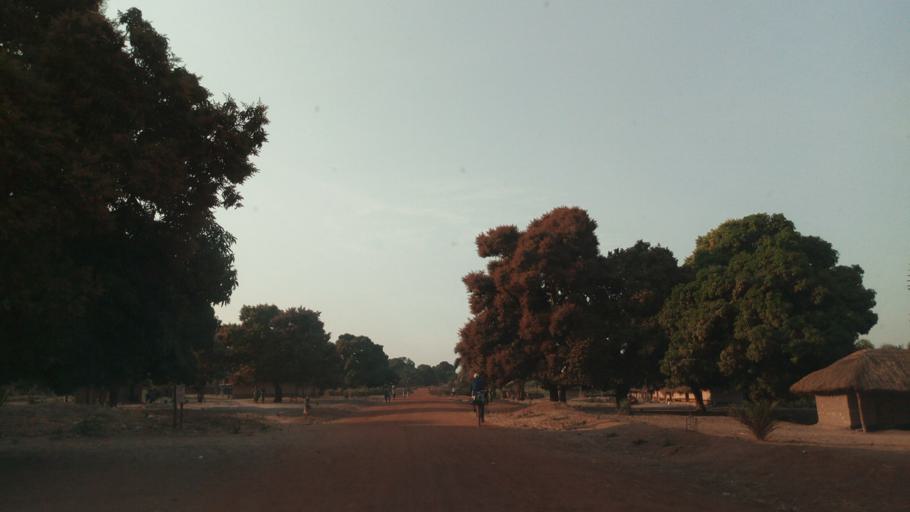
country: ZM
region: Luapula
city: Nchelenge
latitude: -9.6390
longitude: 28.2505
